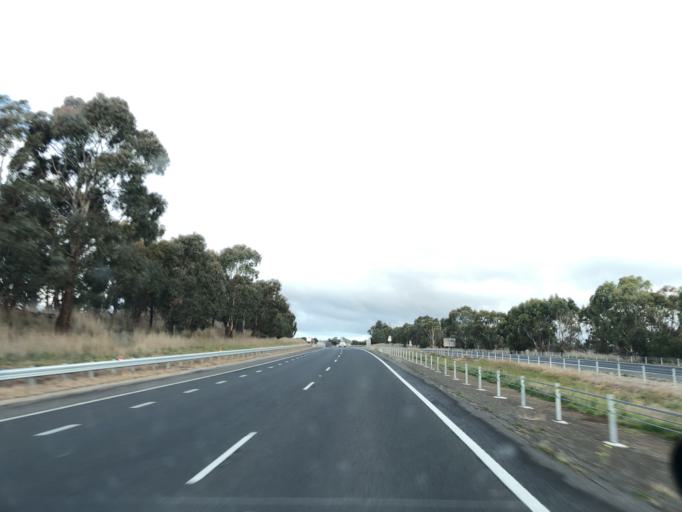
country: AU
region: Victoria
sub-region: Mount Alexander
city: Castlemaine
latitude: -37.2629
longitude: 144.4727
